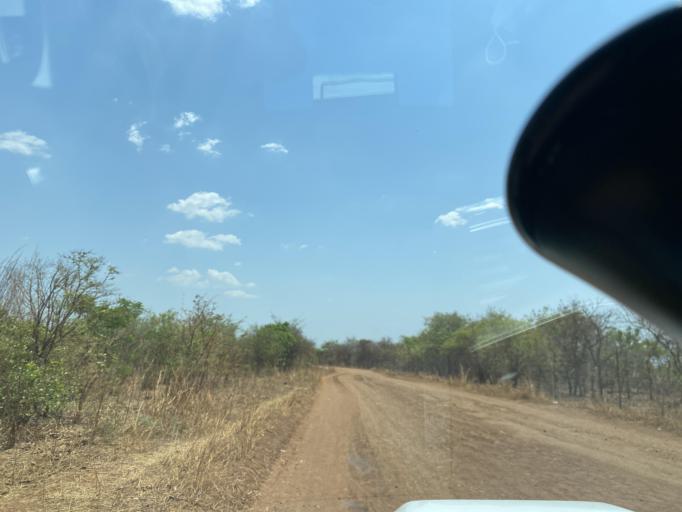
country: ZM
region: Lusaka
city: Lusaka
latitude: -15.5058
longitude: 28.0216
